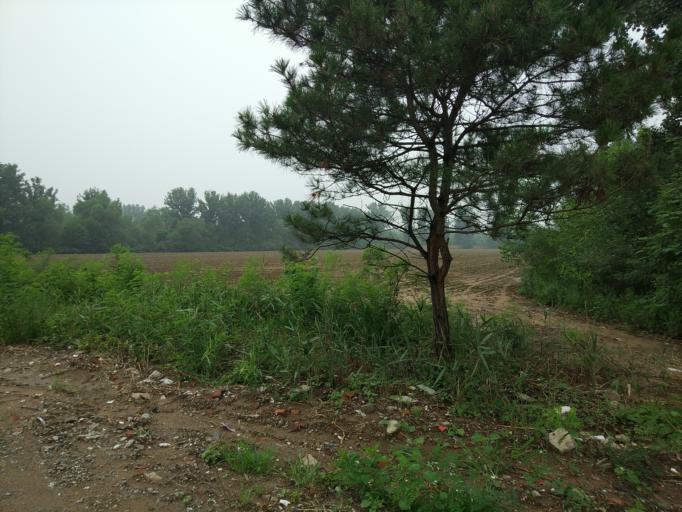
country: CN
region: Beijing
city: Xiaotangshan
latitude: 40.1490
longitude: 116.3586
